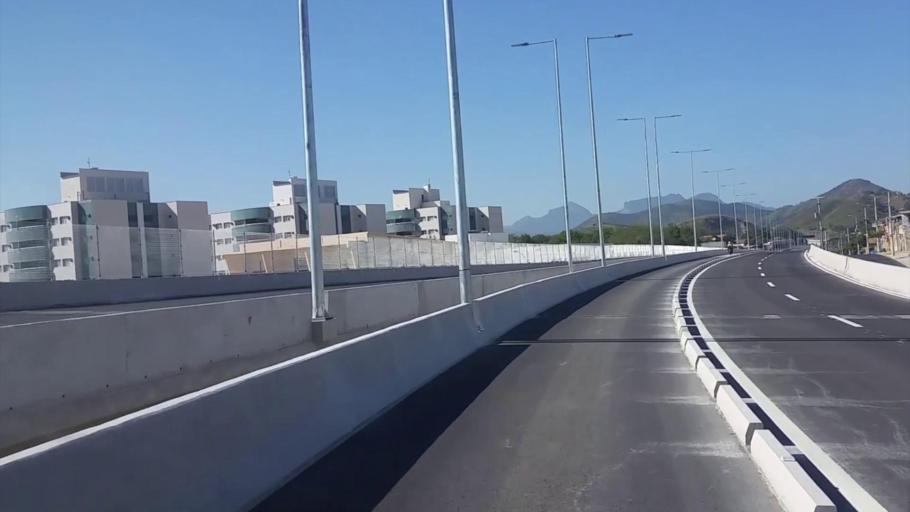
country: BR
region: Rio de Janeiro
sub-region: Nilopolis
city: Nilopolis
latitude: -22.8699
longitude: -43.4112
